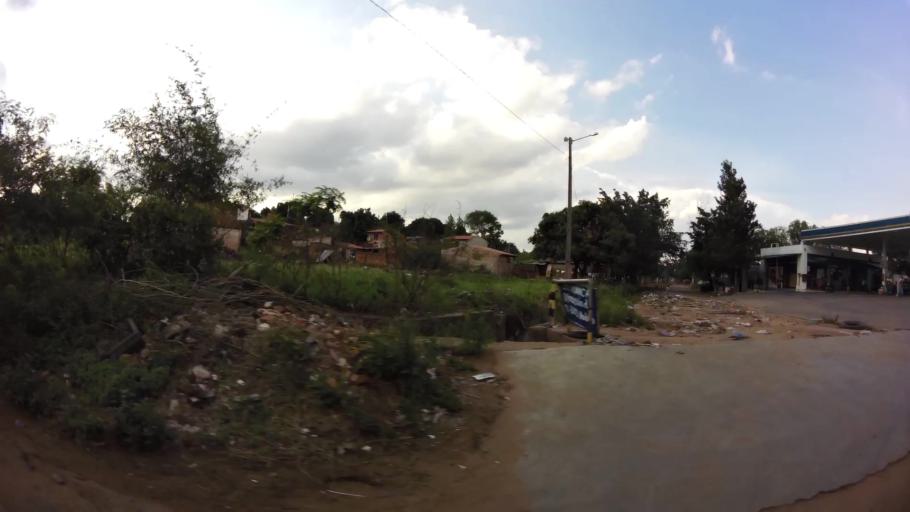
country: PY
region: Central
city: Villa Elisa
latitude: -25.3565
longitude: -57.5597
